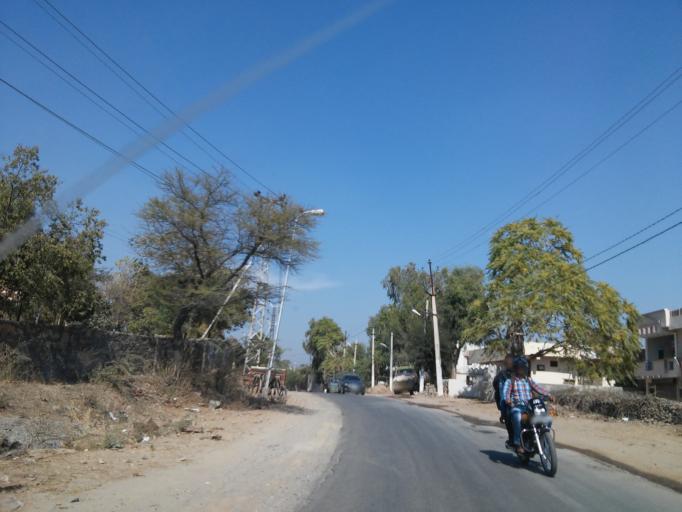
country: IN
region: Rajasthan
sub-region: Udaipur
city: Udaipur
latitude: 24.5751
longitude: 73.6556
